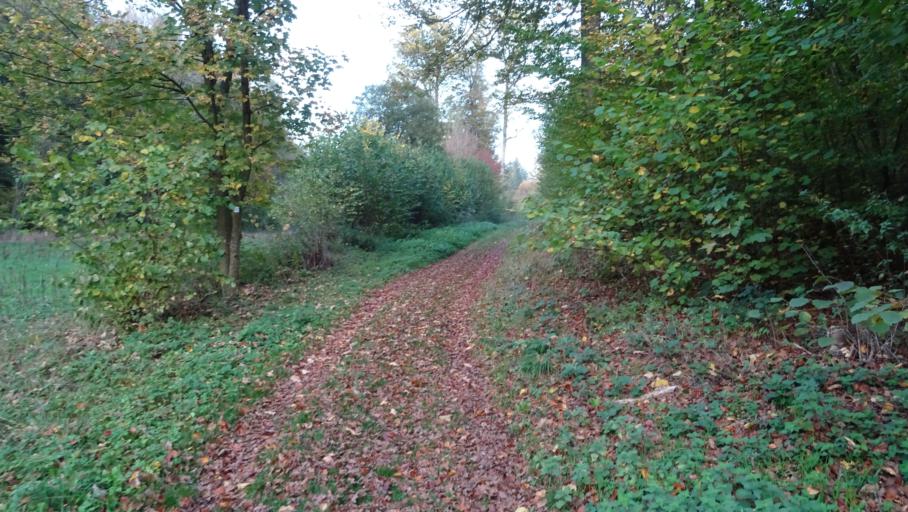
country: DE
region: Baden-Wuerttemberg
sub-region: Karlsruhe Region
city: Obrigheim
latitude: 49.3804
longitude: 9.0876
